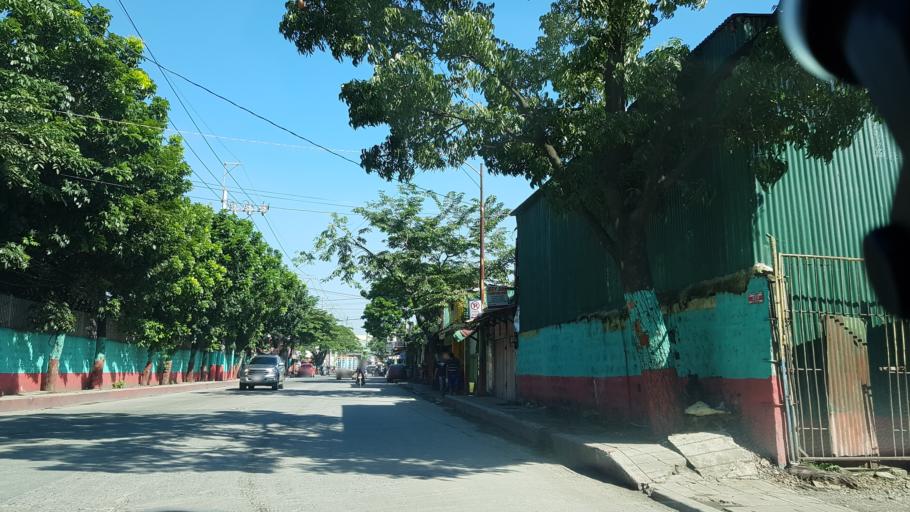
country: PH
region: Calabarzon
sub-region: Province of Rizal
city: Pateros
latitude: 14.5601
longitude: 121.0951
